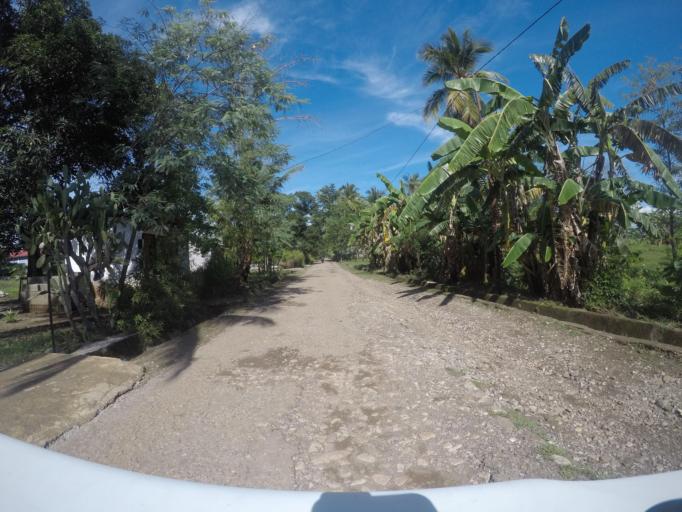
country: TL
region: Bobonaro
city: Maliana
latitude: -8.9882
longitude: 125.2072
